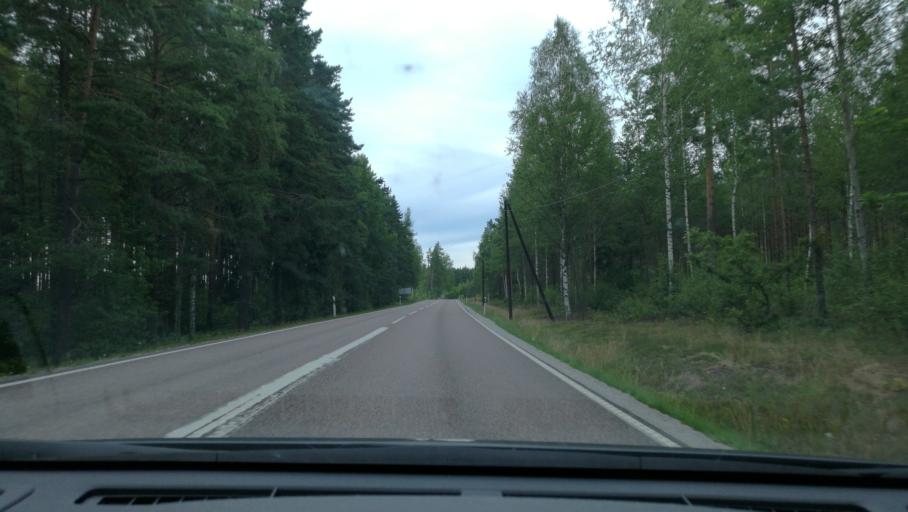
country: SE
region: Vaestmanland
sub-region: Kungsors Kommun
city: Kungsoer
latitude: 59.2897
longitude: 16.1102
